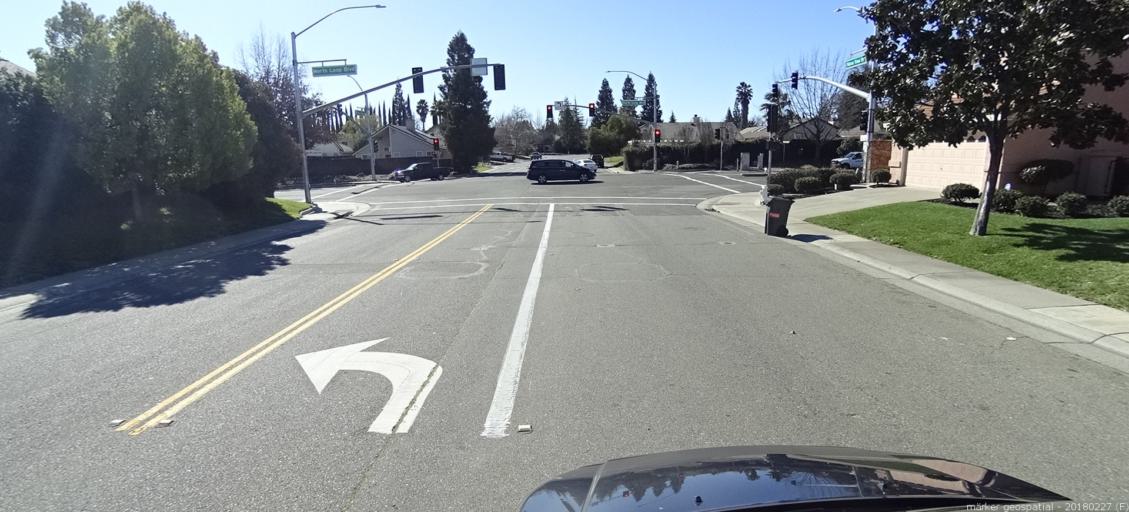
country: US
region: California
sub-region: Sacramento County
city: Antelope
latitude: 38.7188
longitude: -121.3512
